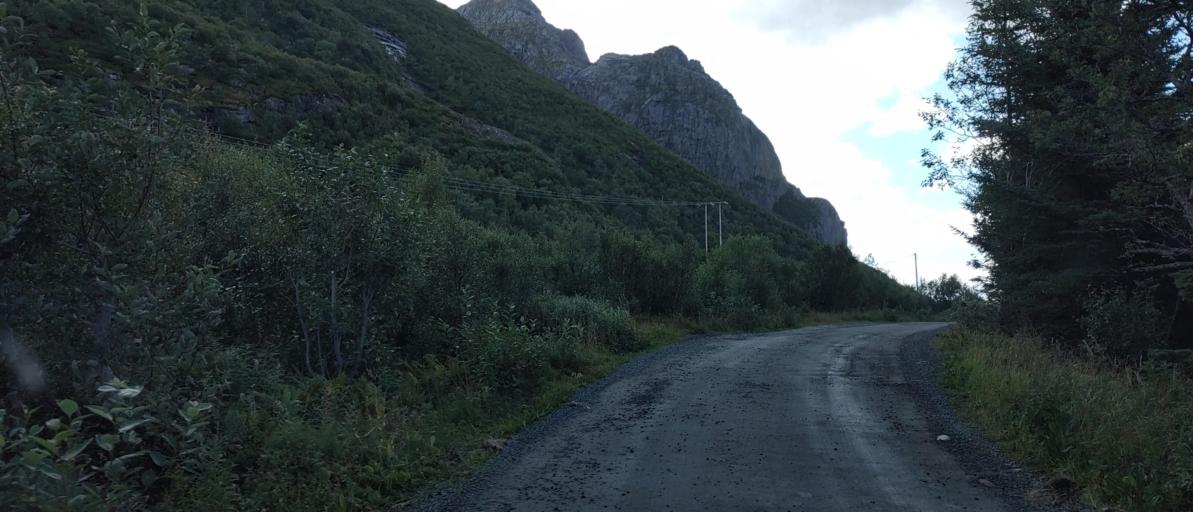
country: NO
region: Nordland
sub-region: Vagan
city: Kabelvag
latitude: 68.2254
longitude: 14.2191
